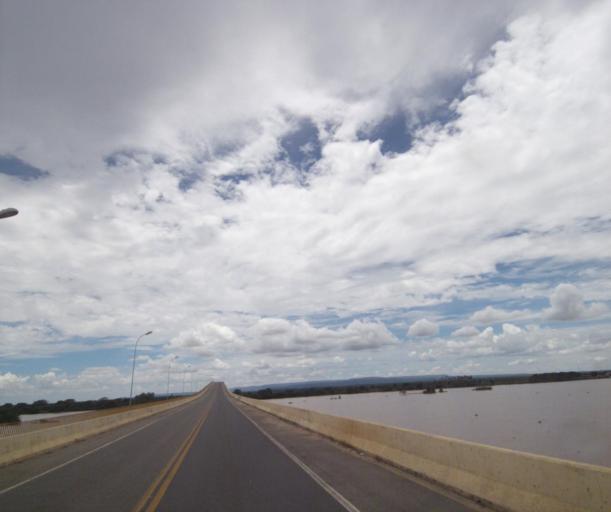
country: BR
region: Bahia
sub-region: Carinhanha
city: Carinhanha
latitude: -14.3231
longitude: -43.7733
